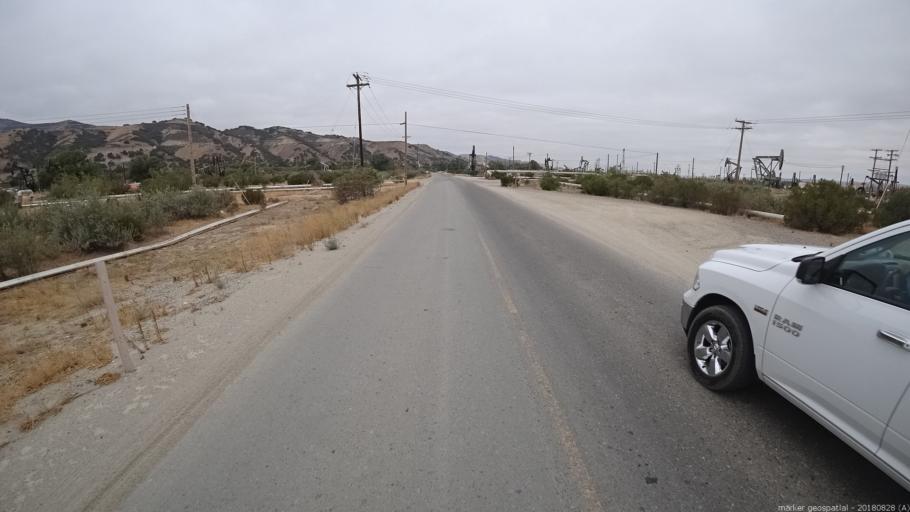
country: US
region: California
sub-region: San Luis Obispo County
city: Lake Nacimiento
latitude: 35.9537
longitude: -120.8707
